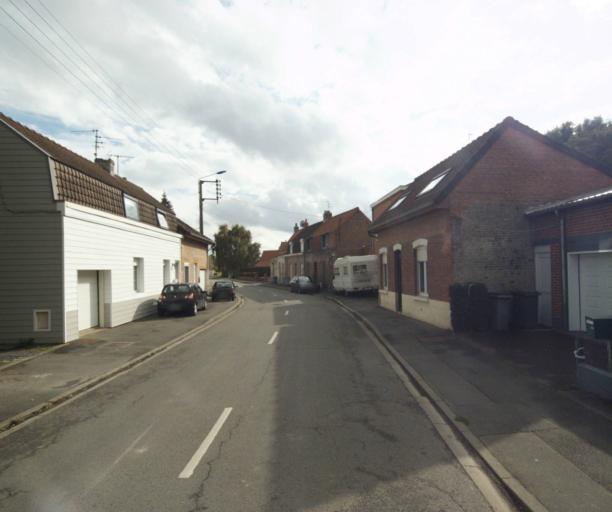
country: FR
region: Nord-Pas-de-Calais
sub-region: Departement du Nord
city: Wavrin
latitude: 50.5720
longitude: 2.9539
